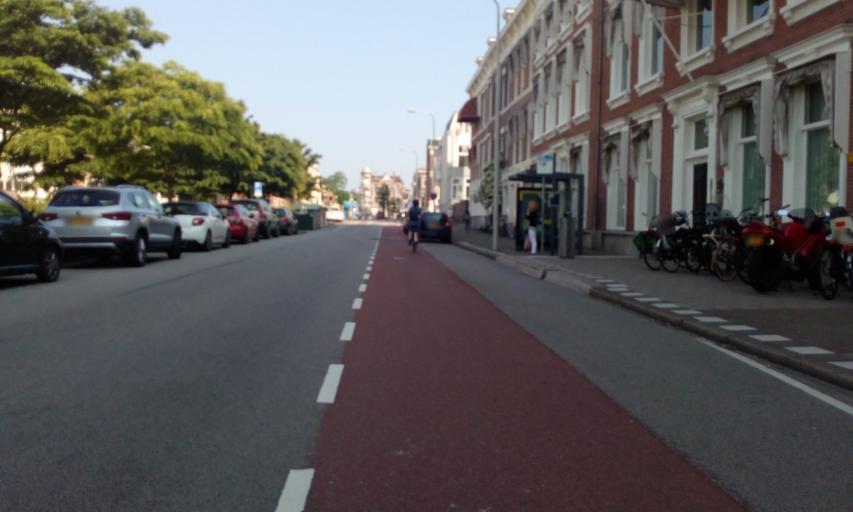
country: NL
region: South Holland
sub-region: Gemeente Den Haag
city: The Hague
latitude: 52.0901
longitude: 4.3058
